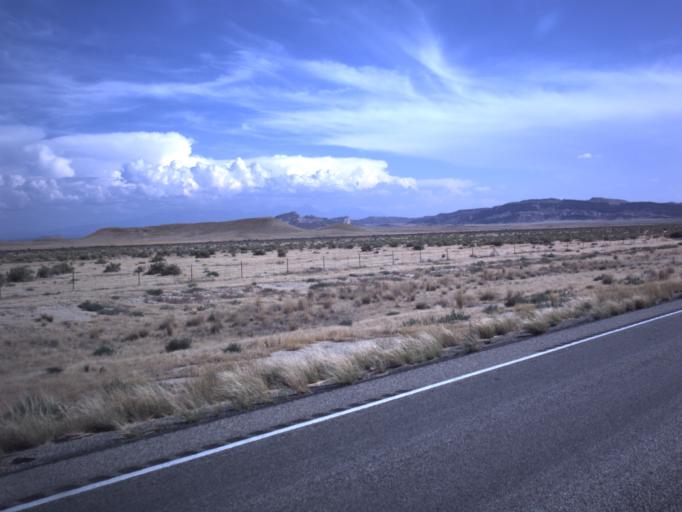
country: US
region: Utah
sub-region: Grand County
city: Moab
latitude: 38.9295
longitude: -109.8158
